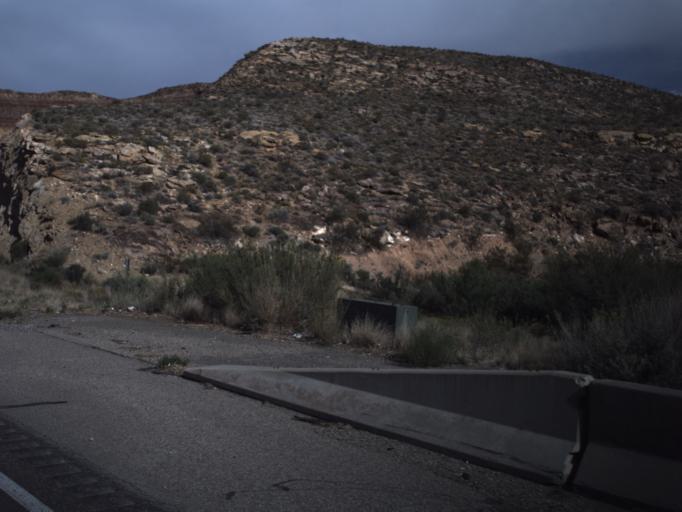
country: US
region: Utah
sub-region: Washington County
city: Hurricane
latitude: 37.1629
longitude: -113.3956
